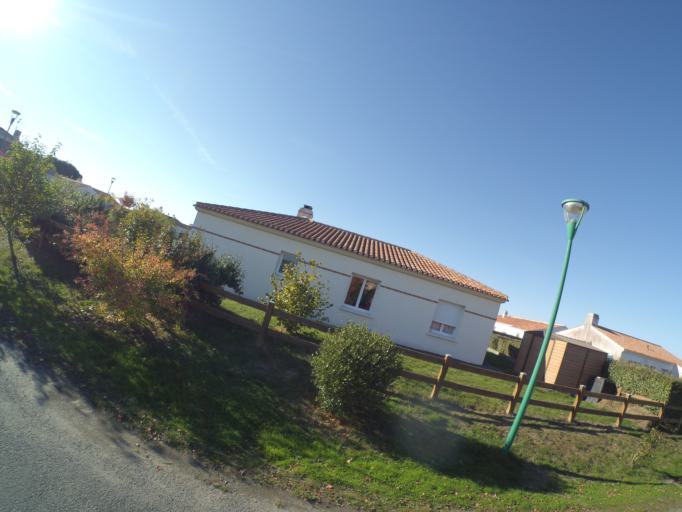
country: FR
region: Pays de la Loire
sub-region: Departement de la Loire-Atlantique
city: Saint-Lumine-de-Clisson
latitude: 47.0844
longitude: -1.3381
